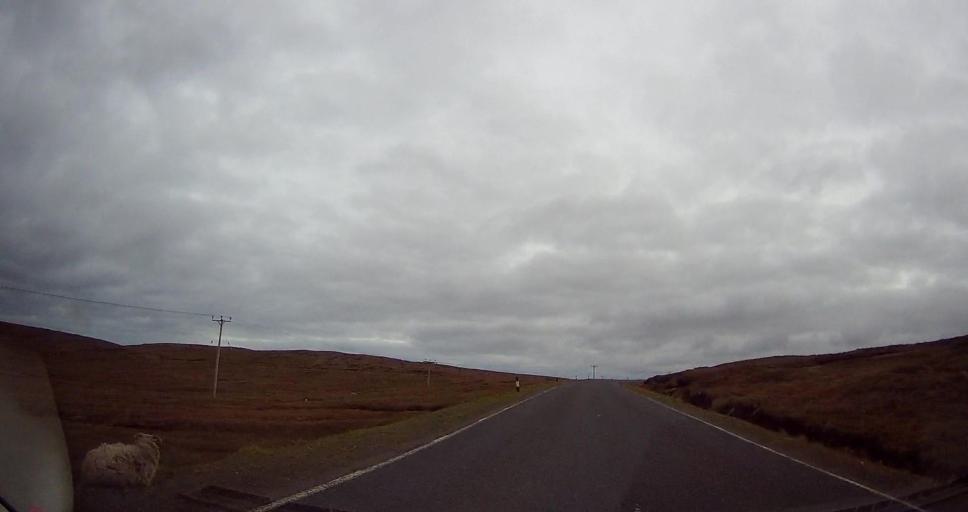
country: GB
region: Scotland
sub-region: Shetland Islands
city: Shetland
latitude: 60.6336
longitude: -1.0662
